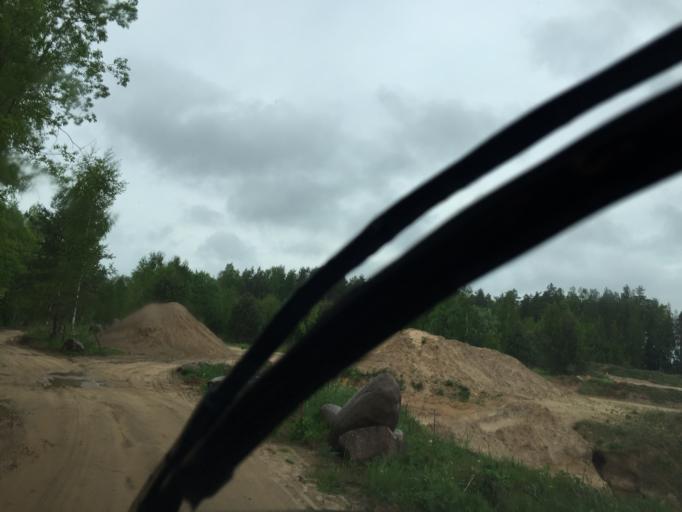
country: LV
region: Kegums
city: Kegums
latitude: 56.7379
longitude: 24.7624
